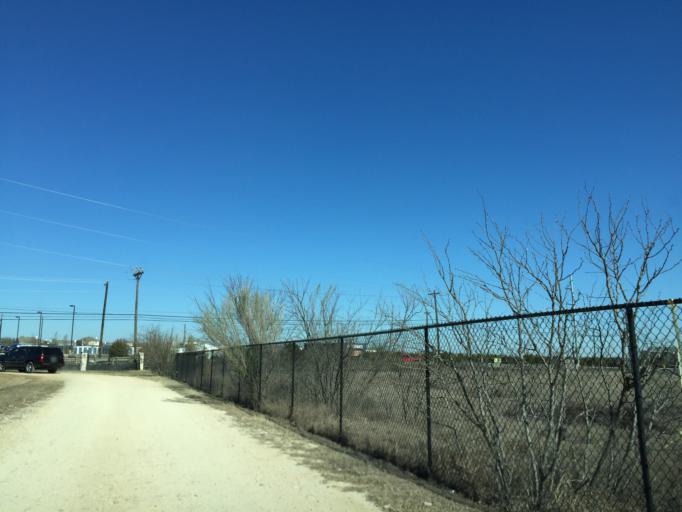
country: US
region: Texas
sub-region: Williamson County
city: Leander
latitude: 30.5771
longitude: -97.8685
